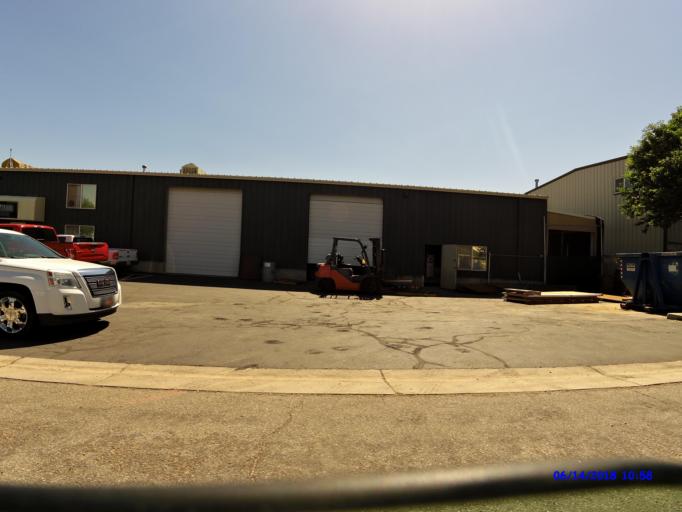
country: US
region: Utah
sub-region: Weber County
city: Riverdale
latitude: 41.2041
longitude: -112.0165
